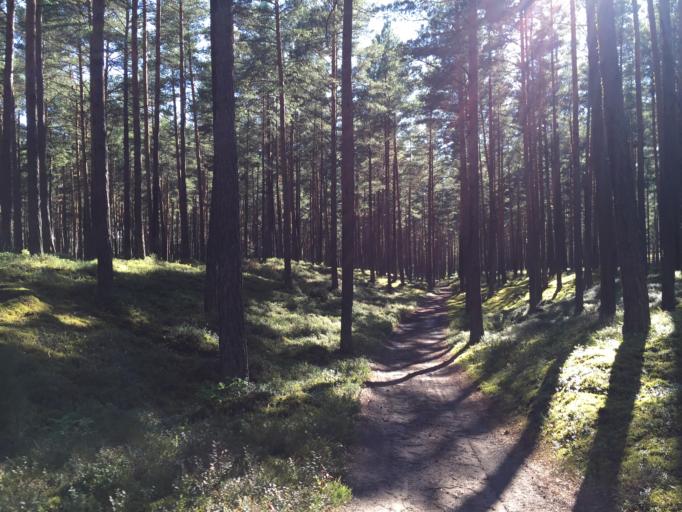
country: LV
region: Riga
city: Jaunciems
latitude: 57.0833
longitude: 24.1427
